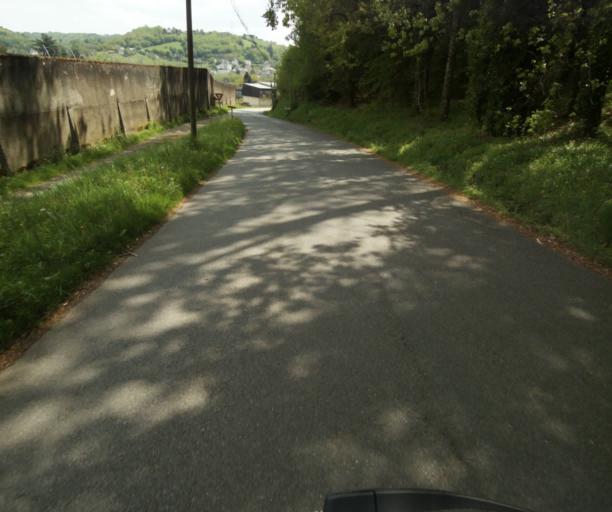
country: FR
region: Limousin
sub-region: Departement de la Correze
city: Tulle
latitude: 45.2752
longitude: 1.7679
